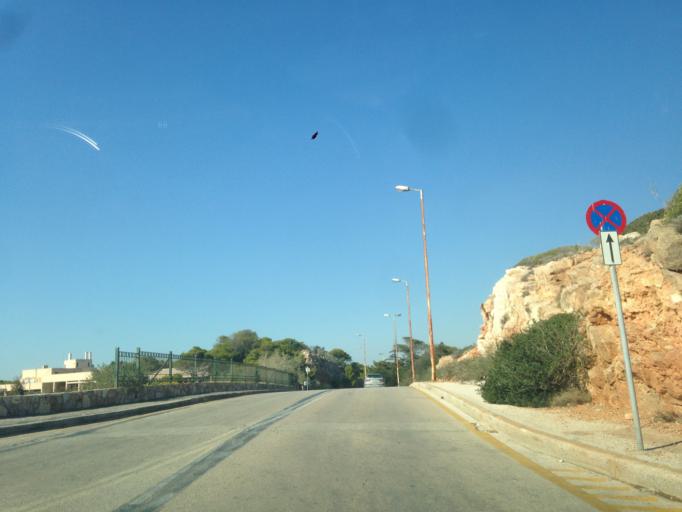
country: GR
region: Attica
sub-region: Nomarchia Anatolikis Attikis
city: Vouliagmeni
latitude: 37.7994
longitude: 23.7721
